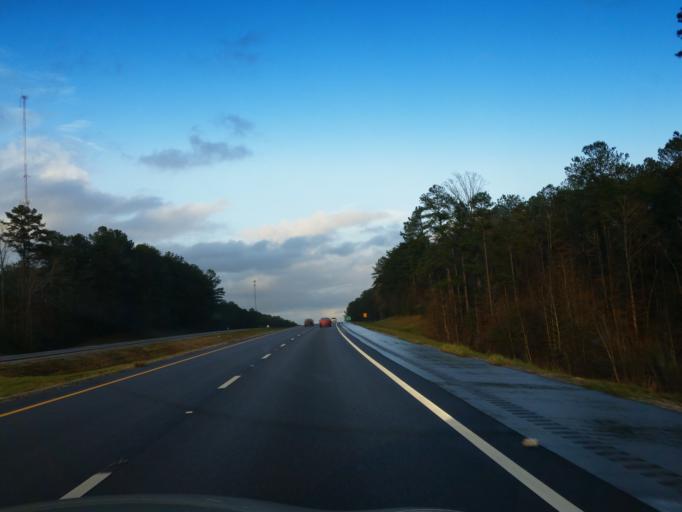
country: US
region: Mississippi
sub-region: Jones County
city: Sharon
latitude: 31.9607
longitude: -88.9715
